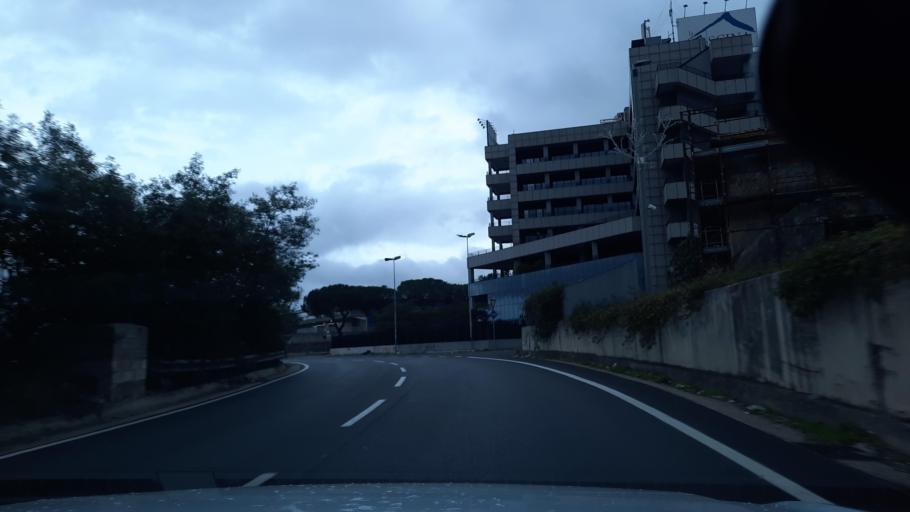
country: IT
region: Latium
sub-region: Citta metropolitana di Roma Capitale
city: Ciampino
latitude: 41.8495
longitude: 12.6061
